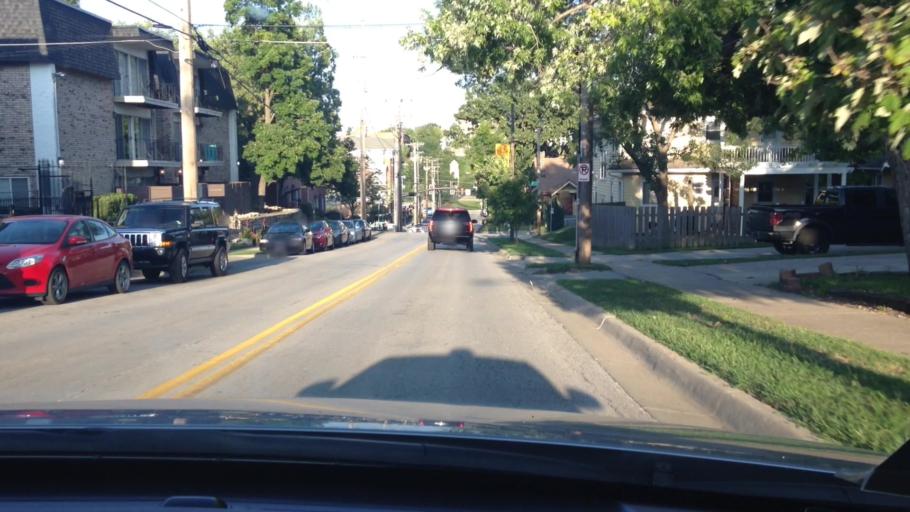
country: US
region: Kansas
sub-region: Johnson County
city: Westwood
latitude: 39.0348
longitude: -94.5859
